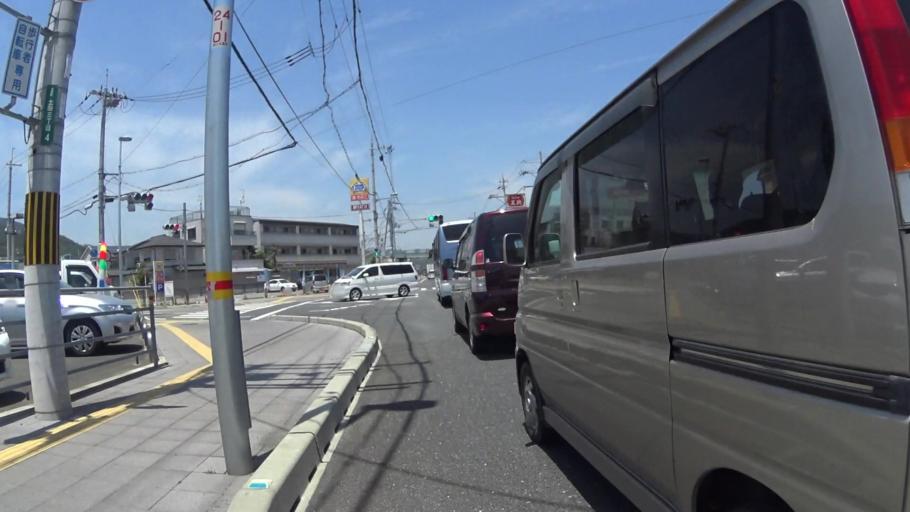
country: JP
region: Kyoto
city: Kameoka
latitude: 35.0356
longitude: 135.5497
